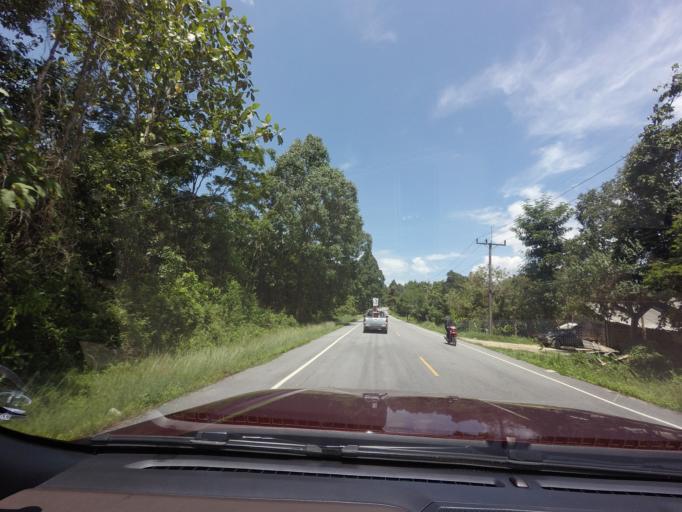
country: TH
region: Narathiwat
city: Chanae
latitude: 6.1399
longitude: 101.7016
